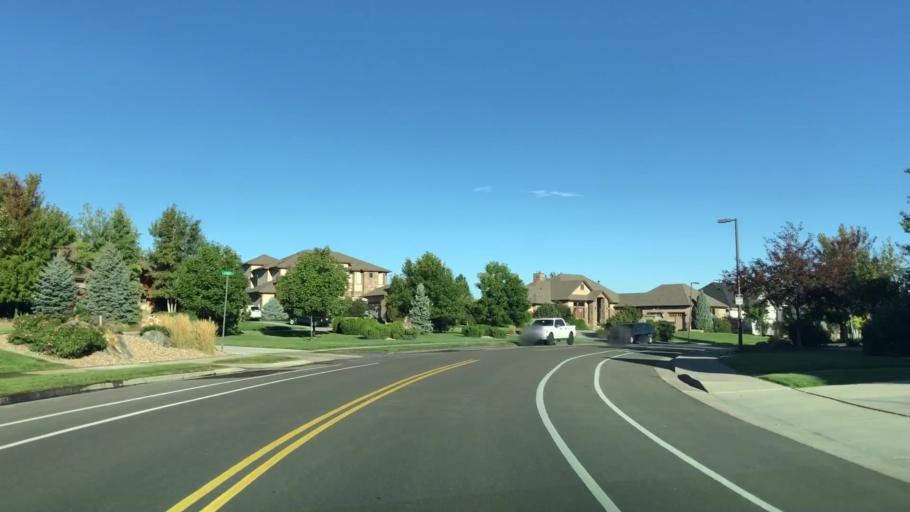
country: US
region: Colorado
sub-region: Larimer County
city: Loveland
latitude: 40.4540
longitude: -105.0313
